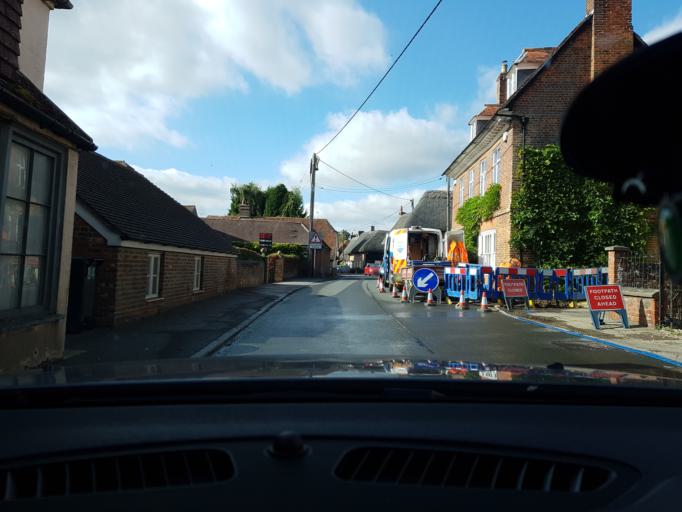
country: GB
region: England
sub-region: Wiltshire
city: Chilton Foliat
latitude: 51.4314
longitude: -1.5379
